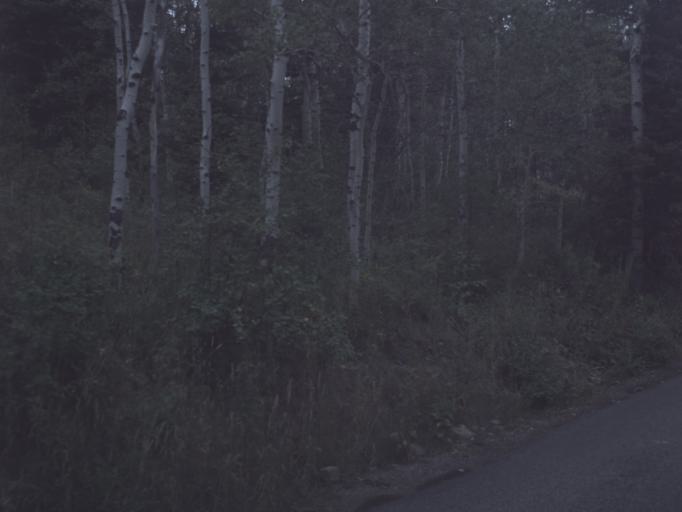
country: US
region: Utah
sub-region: Utah County
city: Lindon
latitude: 40.4143
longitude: -111.6022
